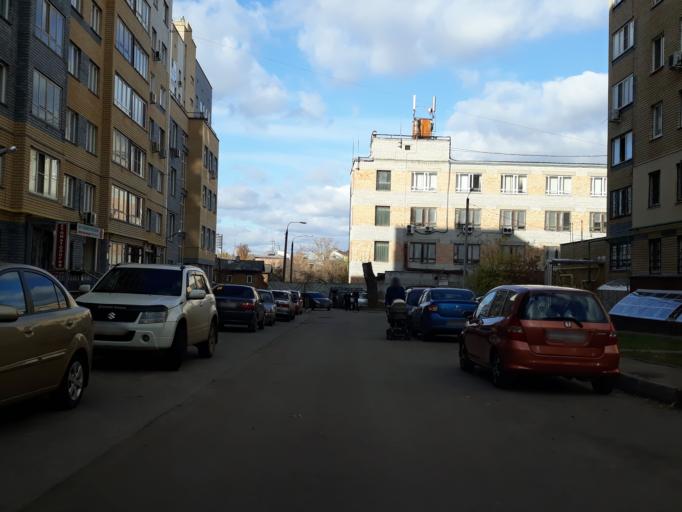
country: RU
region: Nizjnij Novgorod
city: Nizhniy Novgorod
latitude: 56.3035
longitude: 43.9363
